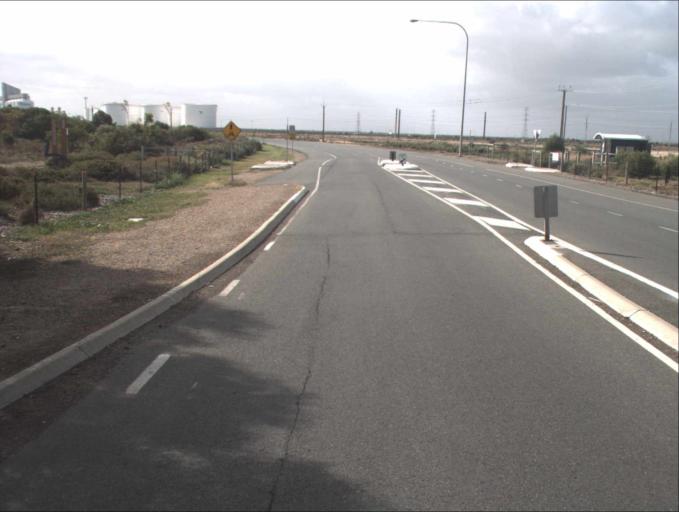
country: AU
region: South Australia
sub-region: Port Adelaide Enfield
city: Birkenhead
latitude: -34.7823
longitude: 138.5004
